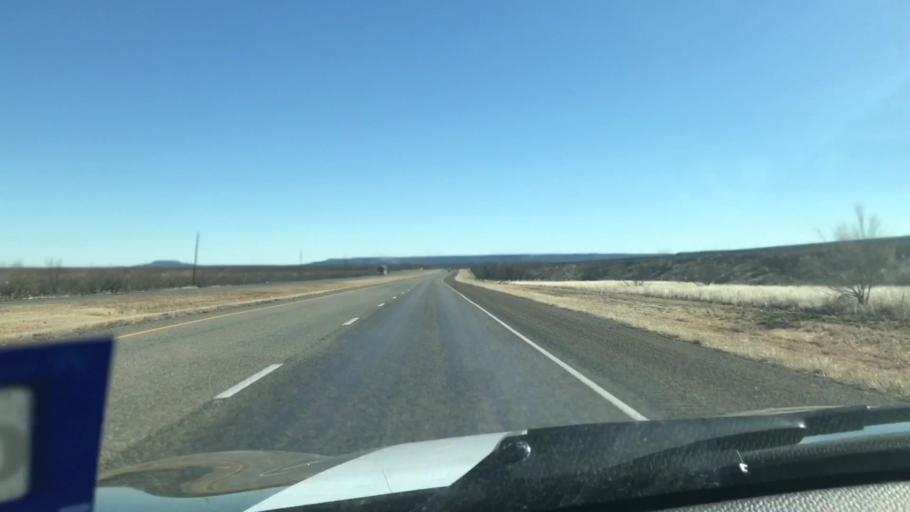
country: US
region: Texas
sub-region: Garza County
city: Post
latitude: 33.0589
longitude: -101.2162
